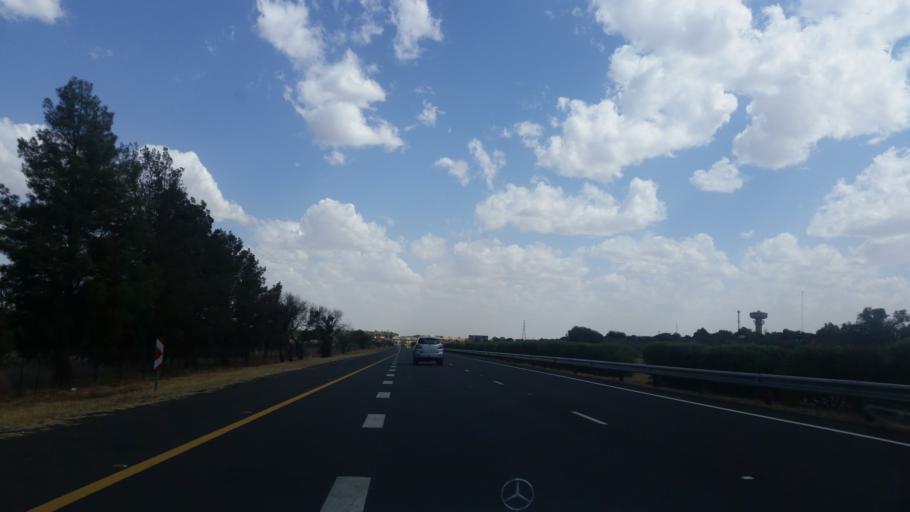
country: ZA
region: Orange Free State
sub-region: Mangaung Metropolitan Municipality
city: Bloemfontein
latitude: -29.0788
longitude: 26.1794
